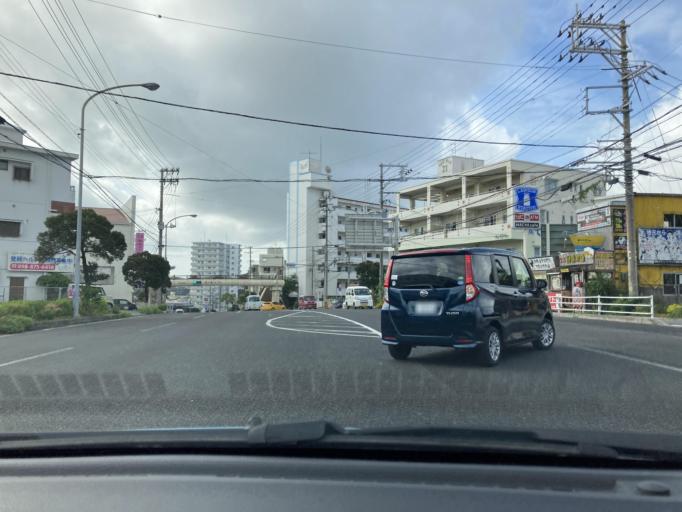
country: JP
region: Okinawa
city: Ginowan
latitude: 26.2521
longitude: 127.7385
